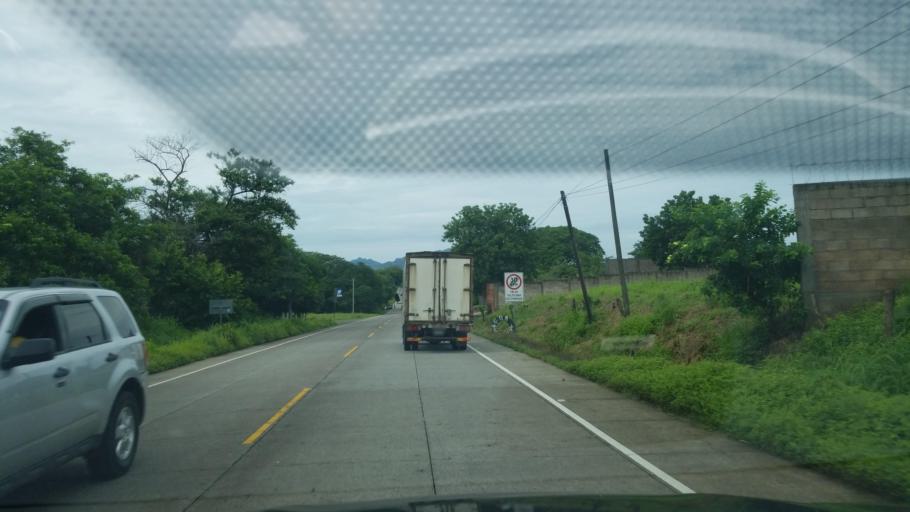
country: HN
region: Choluteca
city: Pespire
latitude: 13.6487
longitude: -87.3682
